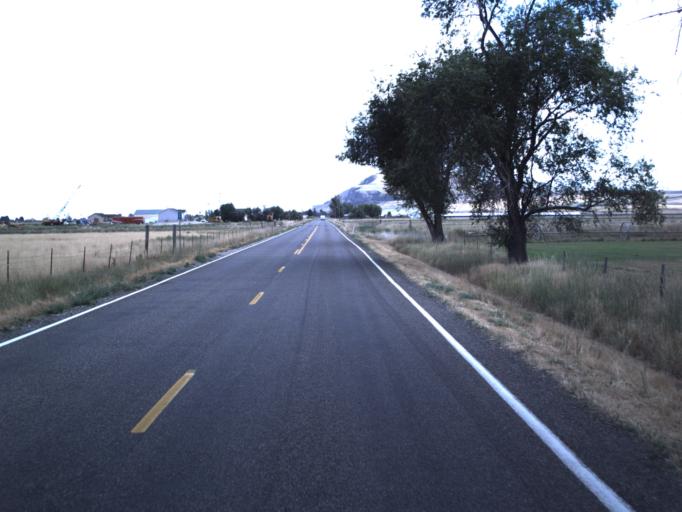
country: US
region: Utah
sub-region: Cache County
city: Lewiston
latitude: 41.9581
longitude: -111.9540
